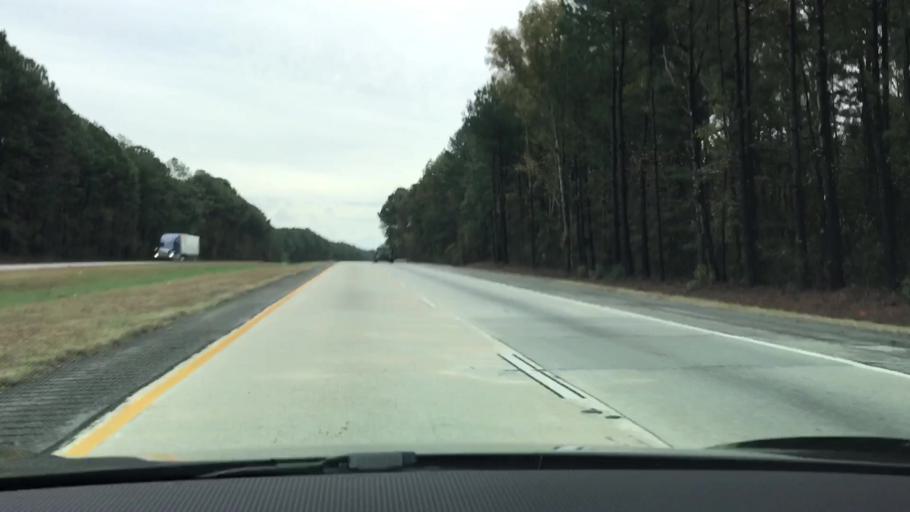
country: US
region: Georgia
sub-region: Greene County
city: Greensboro
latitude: 33.5492
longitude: -83.1396
